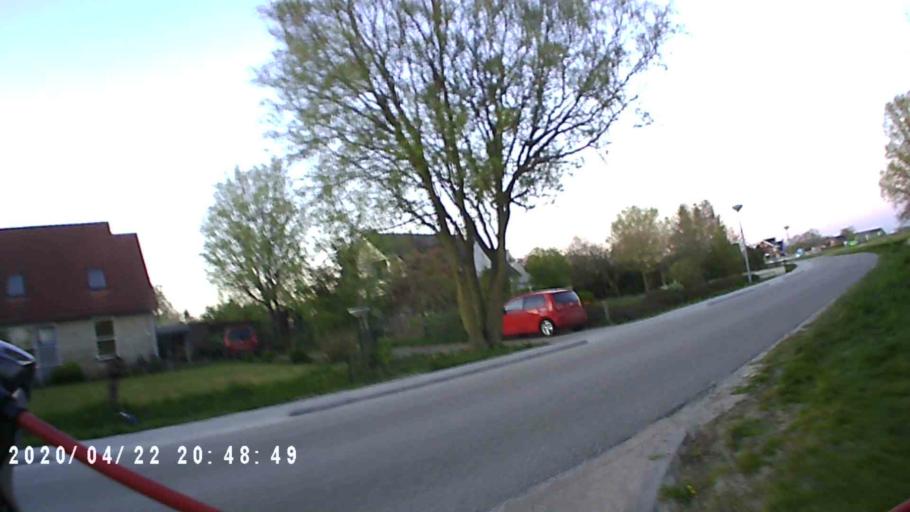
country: NL
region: Groningen
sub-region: Gemeente Winsum
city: Winsum
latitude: 53.3311
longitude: 6.5287
